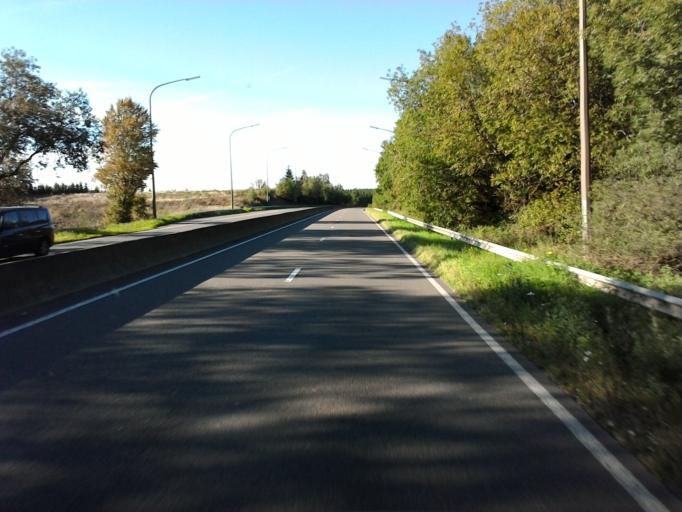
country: BE
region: Wallonia
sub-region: Province du Luxembourg
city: Fauvillers
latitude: 49.8793
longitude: 5.7047
